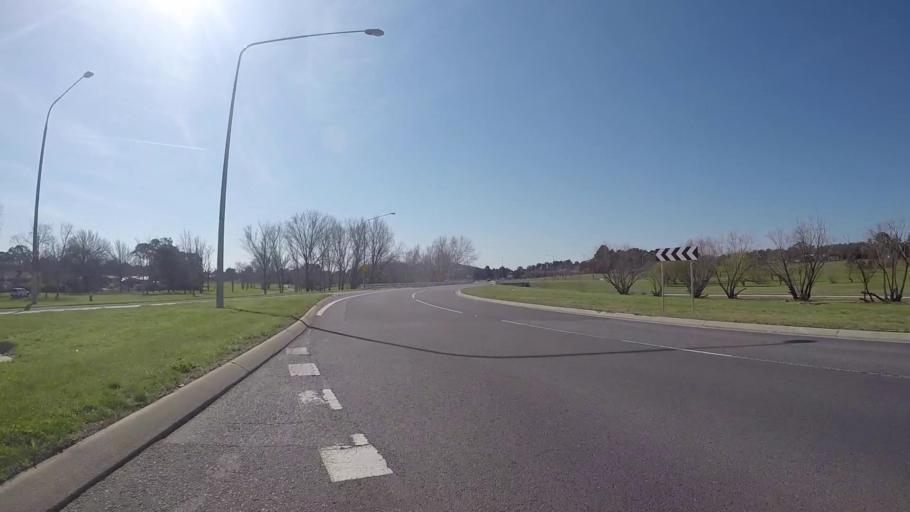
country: AU
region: Australian Capital Territory
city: Forrest
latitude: -35.3362
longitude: 149.0855
